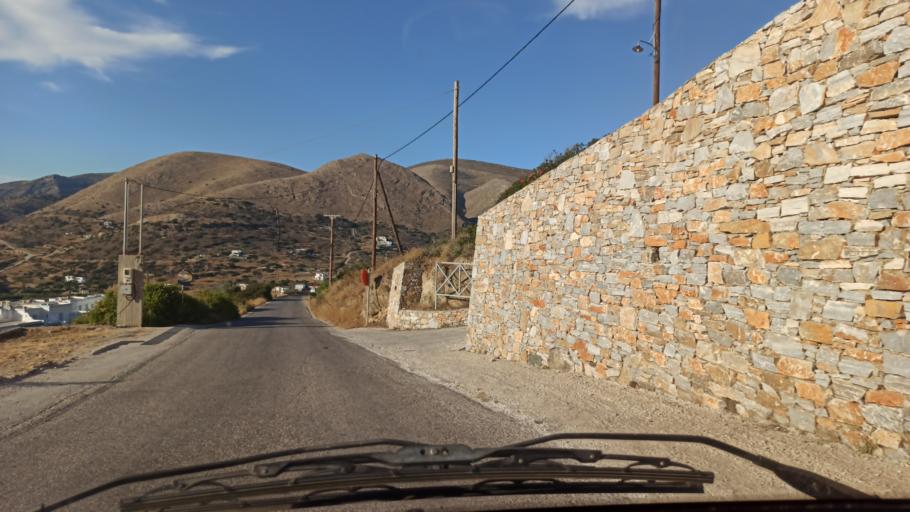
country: GR
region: South Aegean
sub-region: Nomos Kykladon
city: Ano Syros
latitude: 37.4407
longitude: 24.9021
